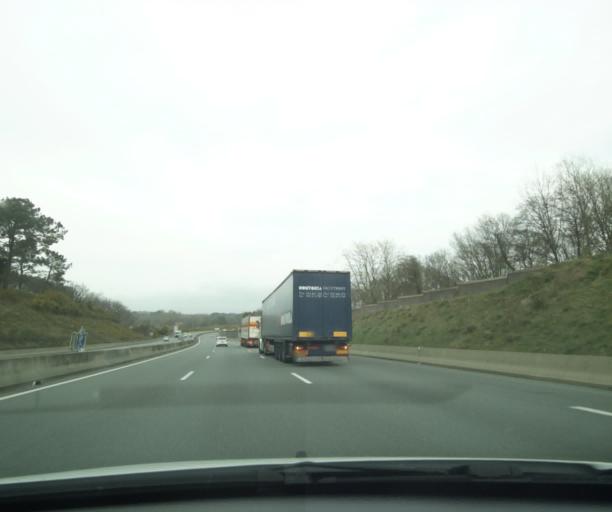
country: FR
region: Aquitaine
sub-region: Departement des Pyrenees-Atlantiques
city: Bassussarry
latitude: 43.4566
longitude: -1.5232
